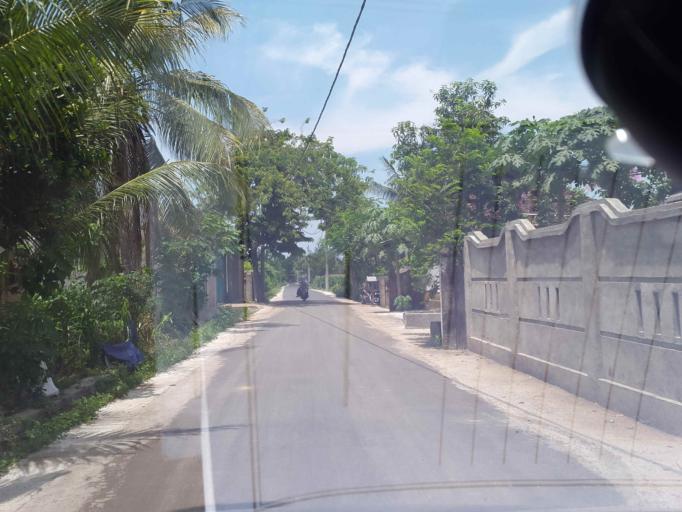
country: ID
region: West Nusa Tenggara
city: Jelateng Timur
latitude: -8.7089
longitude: 116.0772
